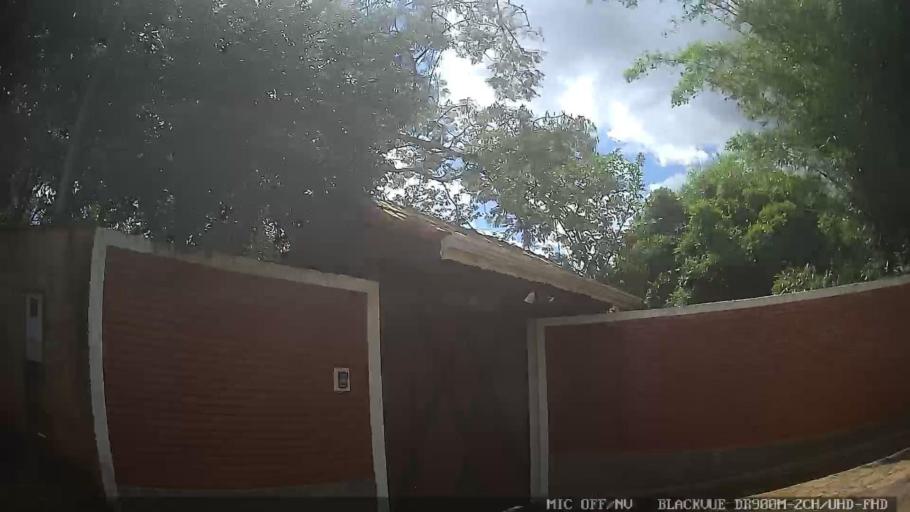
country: BR
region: Minas Gerais
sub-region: Extrema
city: Extrema
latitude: -22.8689
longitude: -46.3437
